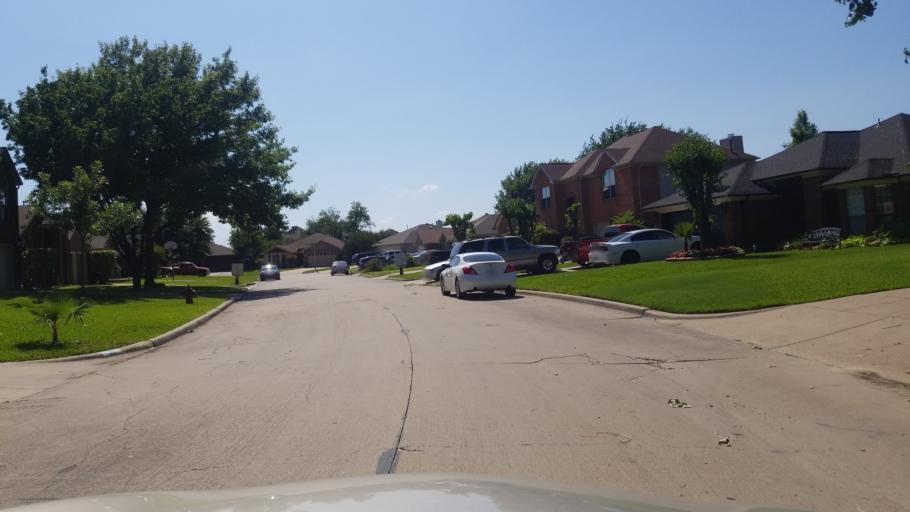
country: US
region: Texas
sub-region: Dallas County
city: Grand Prairie
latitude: 32.6913
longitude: -97.0132
